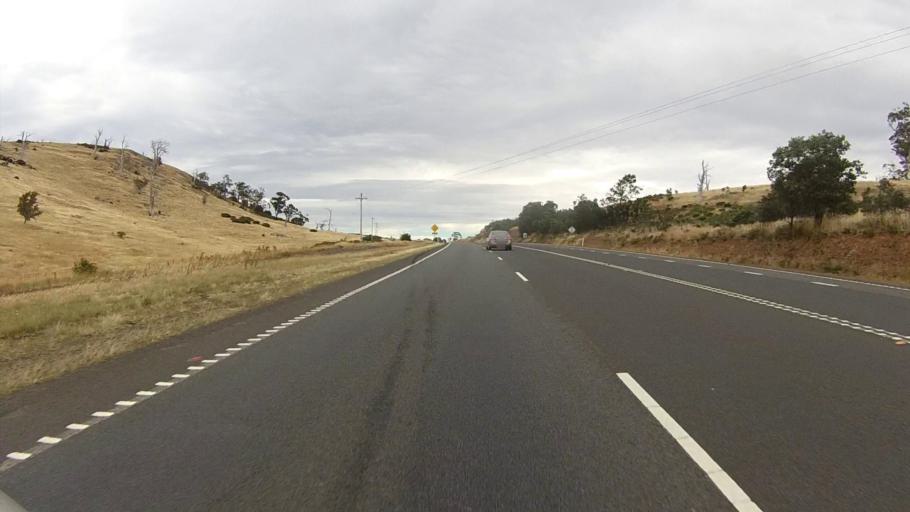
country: AU
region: Tasmania
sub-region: Brighton
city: Bridgewater
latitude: -42.3387
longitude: 147.3418
